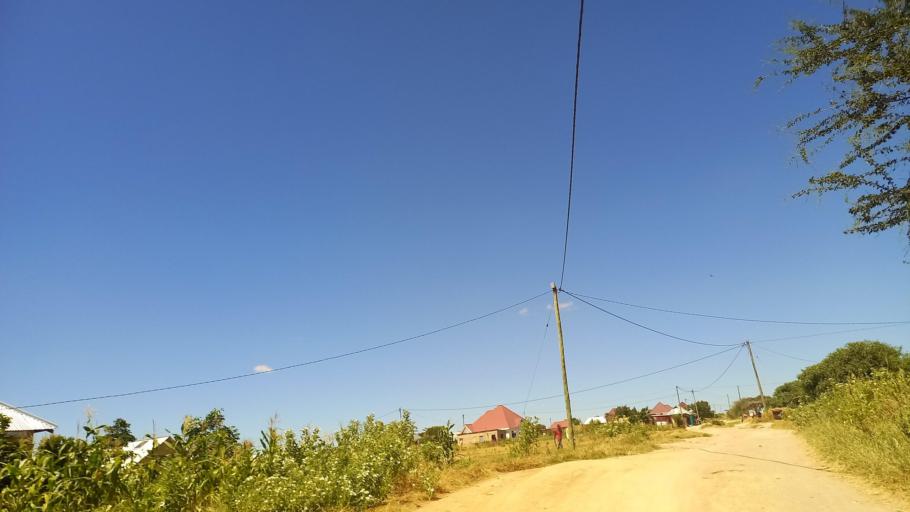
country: TZ
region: Dodoma
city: Dodoma
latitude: -6.1283
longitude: 35.6965
